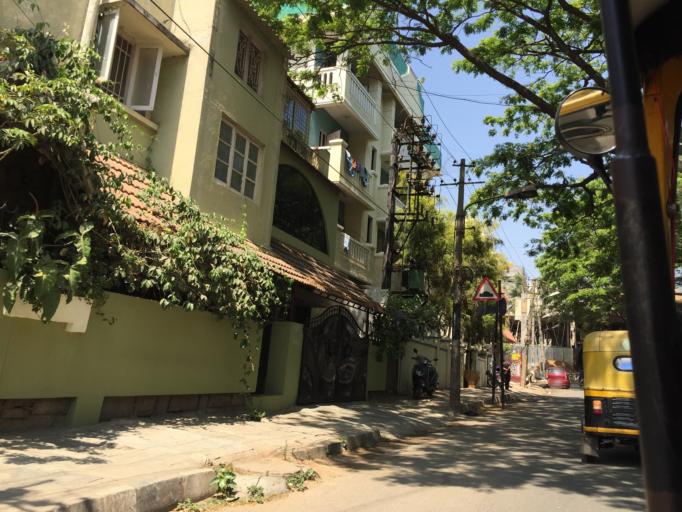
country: IN
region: Karnataka
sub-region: Bangalore Urban
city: Bangalore
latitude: 12.9987
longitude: 77.6179
